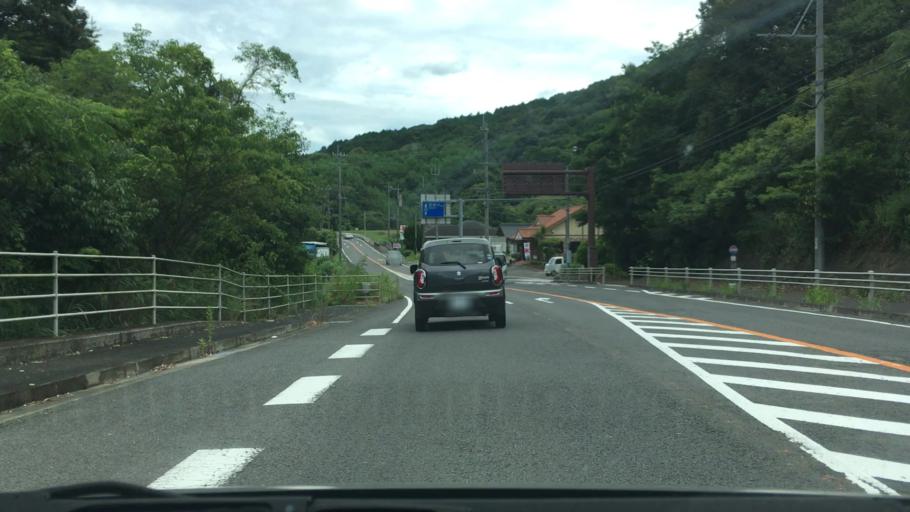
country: JP
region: Nagasaki
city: Sasebo
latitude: 32.9959
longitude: 129.7326
